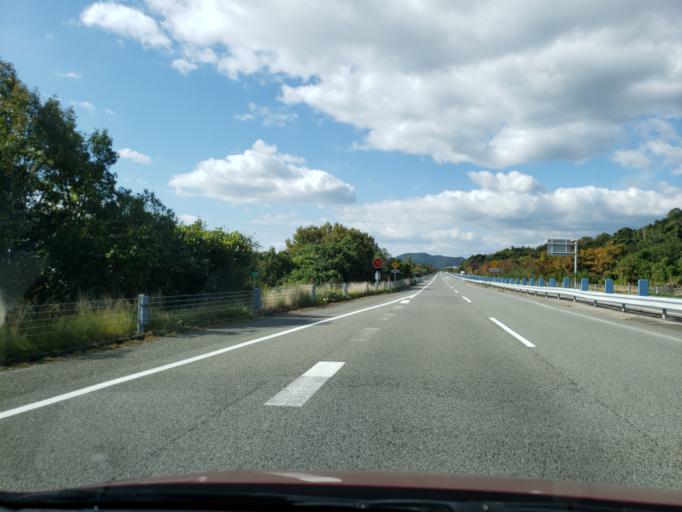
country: JP
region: Tokushima
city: Kamojimacho-jogejima
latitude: 34.1205
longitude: 134.3528
